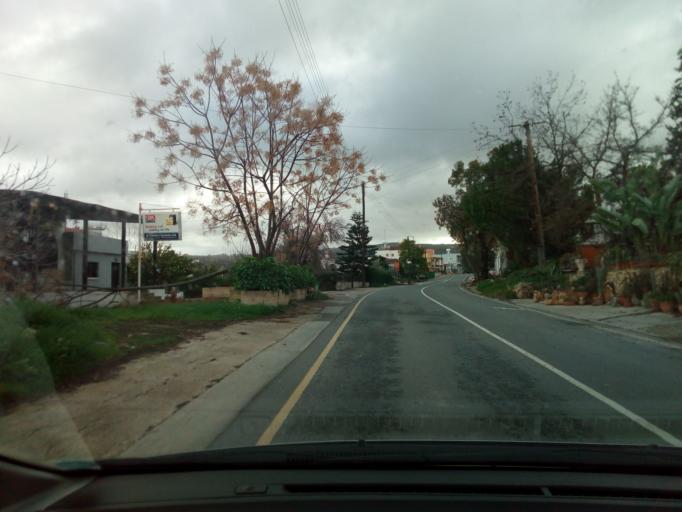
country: CY
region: Pafos
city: Tala
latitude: 34.9226
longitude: 32.4778
